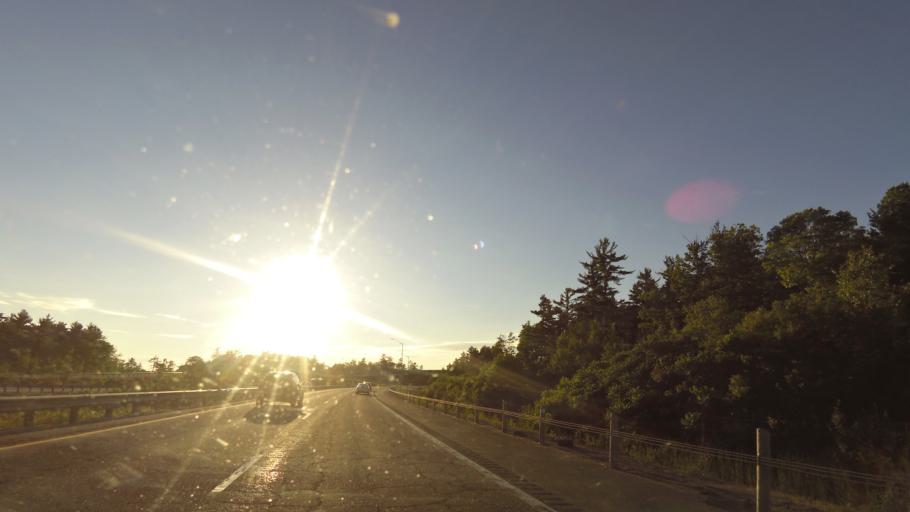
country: CA
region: Ontario
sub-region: Parry Sound District
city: Parry Sound
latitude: 45.3447
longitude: -79.9995
